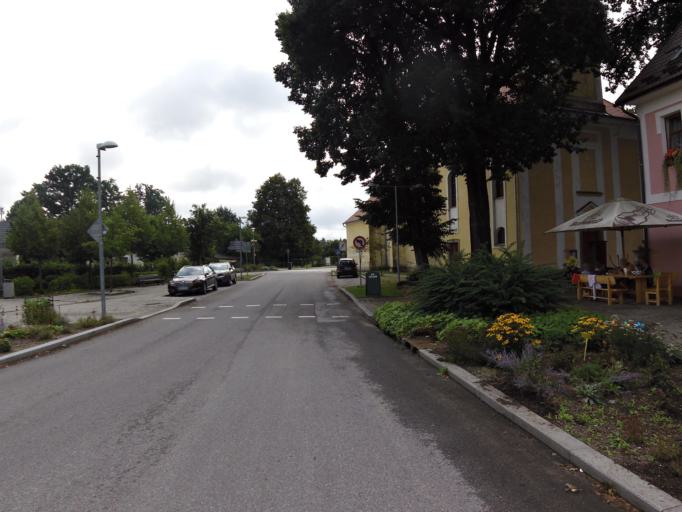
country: CZ
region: Jihocesky
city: Suchdol nad Luznici
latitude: 48.8880
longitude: 14.8747
